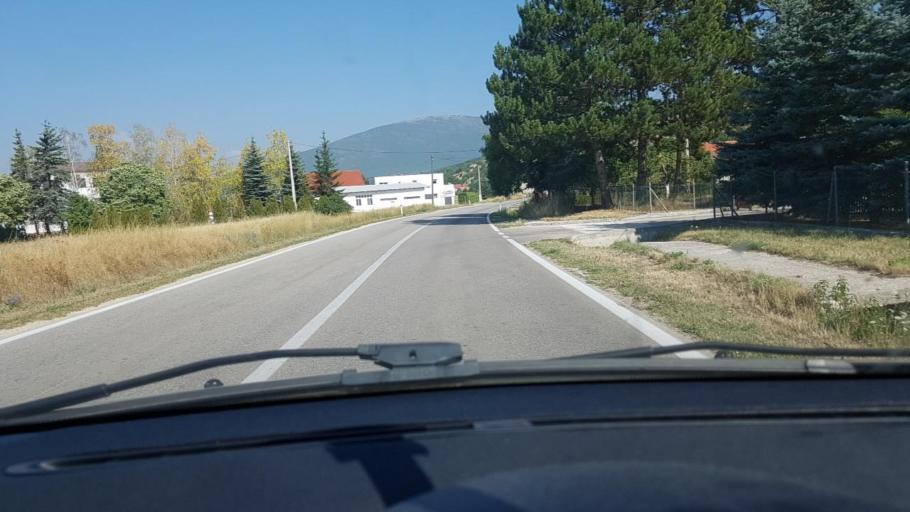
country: BA
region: Federation of Bosnia and Herzegovina
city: Zabrisce
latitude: 43.8505
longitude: 16.9531
